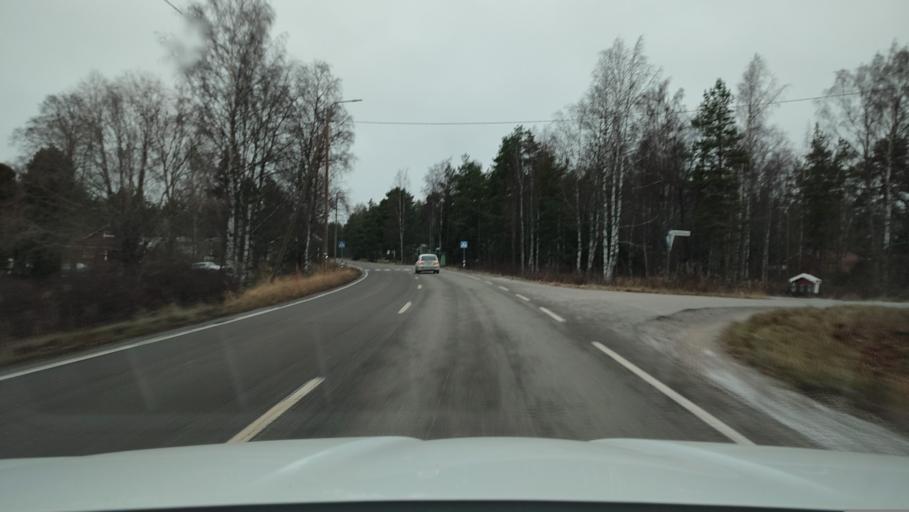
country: FI
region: Ostrobothnia
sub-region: Sydosterbotten
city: Naerpes
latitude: 62.3941
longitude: 21.3719
